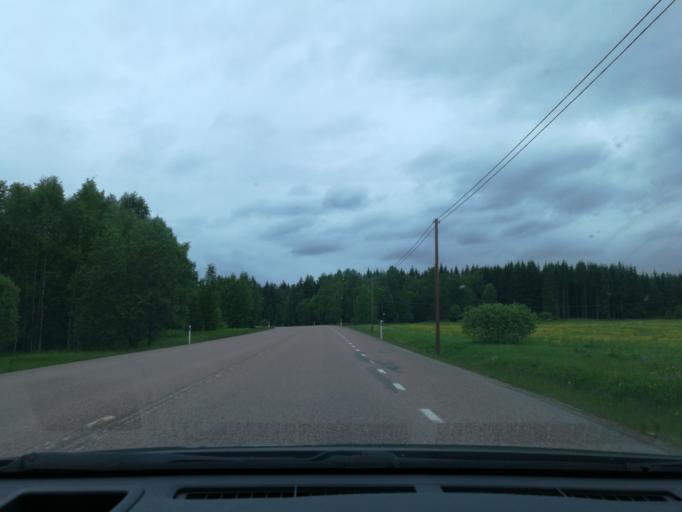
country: SE
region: Dalarna
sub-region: Ludvika Kommun
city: Ludvika
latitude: 60.1427
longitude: 15.2974
